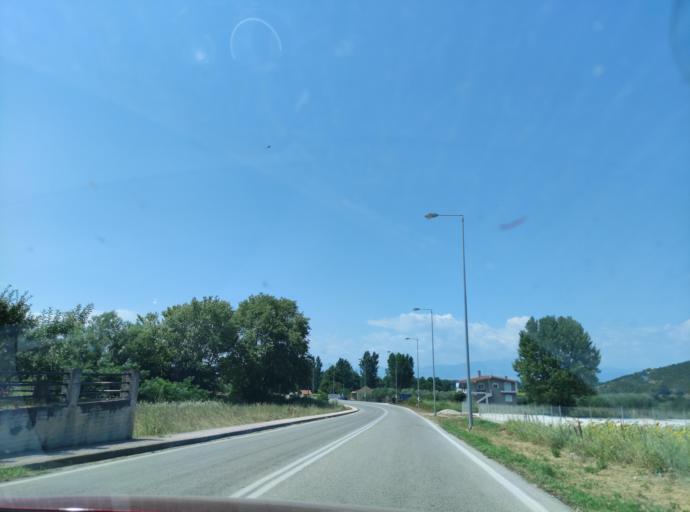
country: GR
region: East Macedonia and Thrace
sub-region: Nomos Kavalas
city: Palaiochori
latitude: 40.9486
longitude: 24.2085
